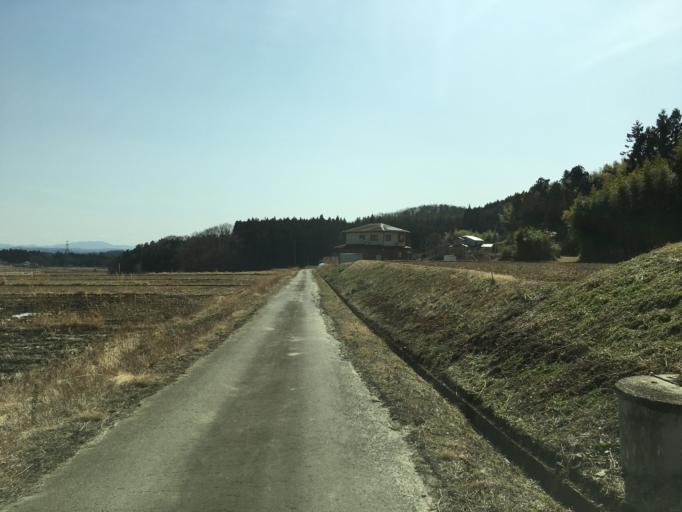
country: JP
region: Fukushima
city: Nihommatsu
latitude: 37.5886
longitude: 140.3763
